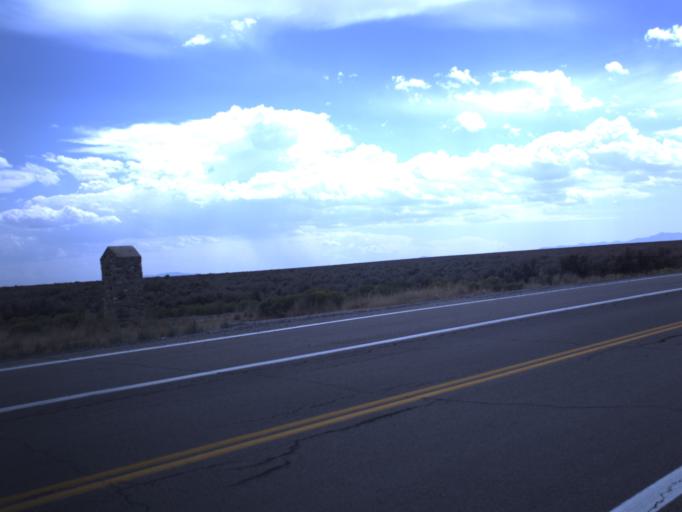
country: US
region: Utah
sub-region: Tooele County
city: Tooele
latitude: 40.3808
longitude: -112.3869
